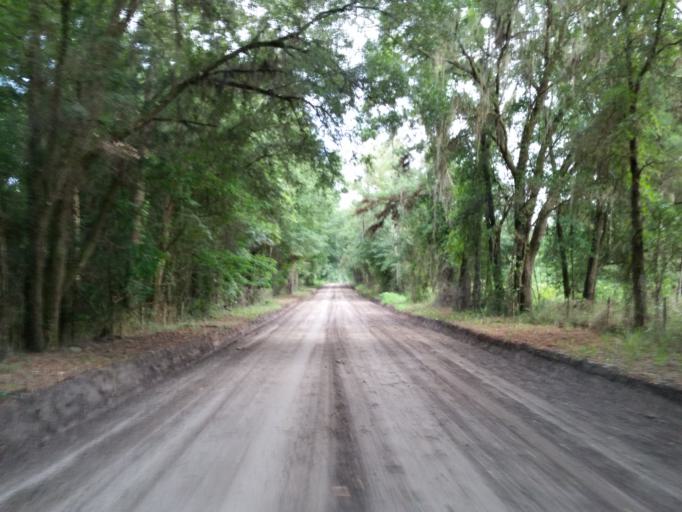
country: US
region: Florida
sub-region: Alachua County
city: High Springs
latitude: 29.9661
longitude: -82.5595
